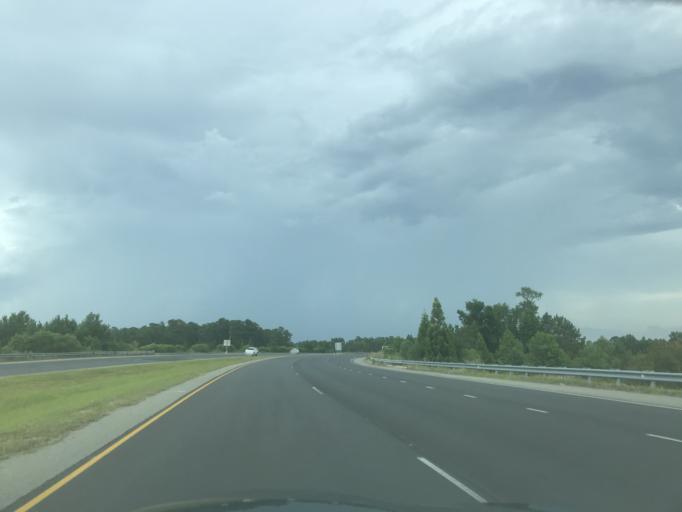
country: US
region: North Carolina
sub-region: Johnston County
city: Wilsons Mills
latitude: 35.6003
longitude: -78.4131
